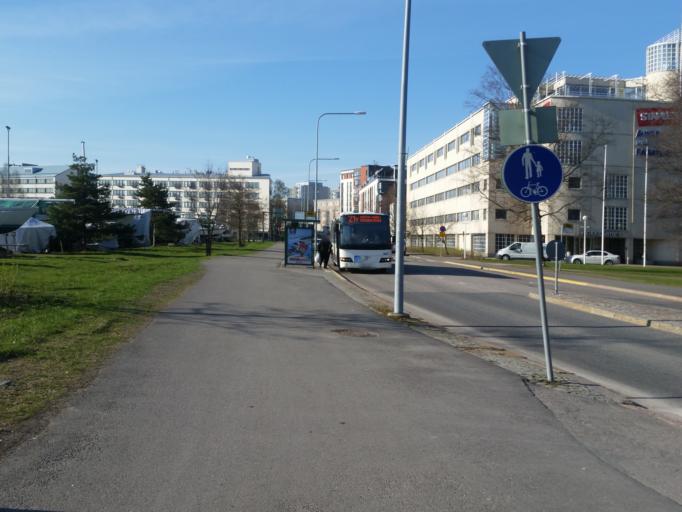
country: FI
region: Uusimaa
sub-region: Helsinki
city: Helsinki
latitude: 60.1569
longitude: 24.8858
